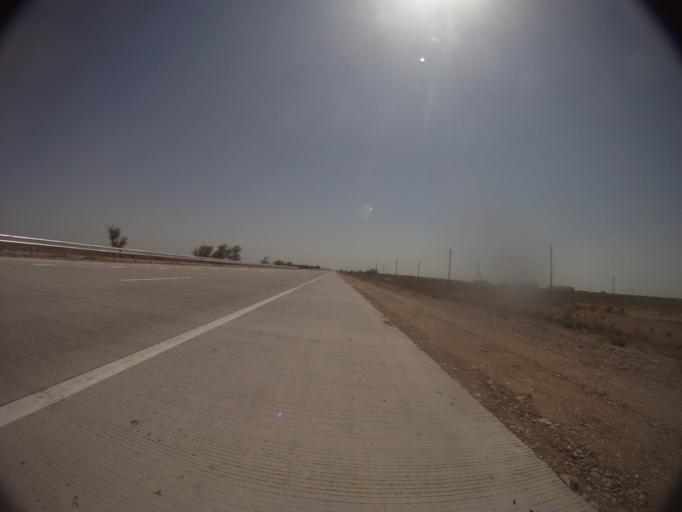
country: KZ
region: Ongtustik Qazaqstan
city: Bayaldyr
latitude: 43.0734
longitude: 68.6617
